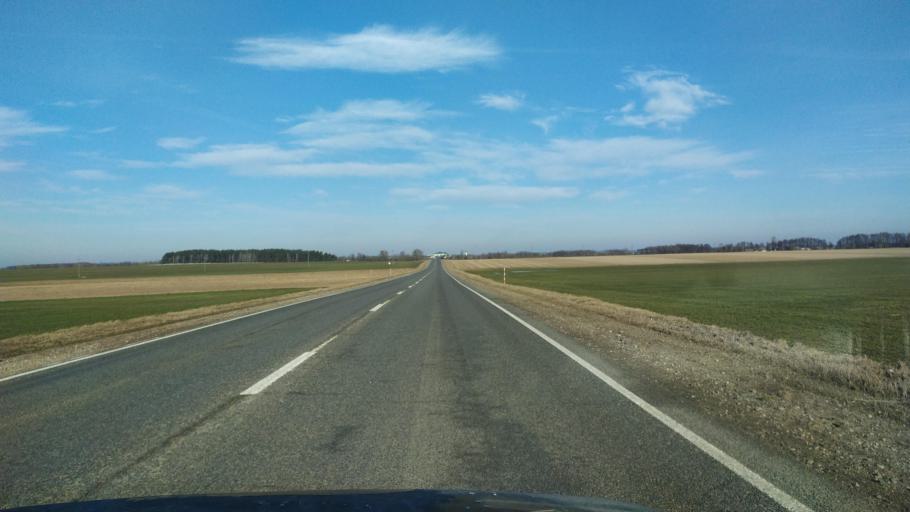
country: BY
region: Brest
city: Kamyanyets
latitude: 52.3744
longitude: 23.7916
